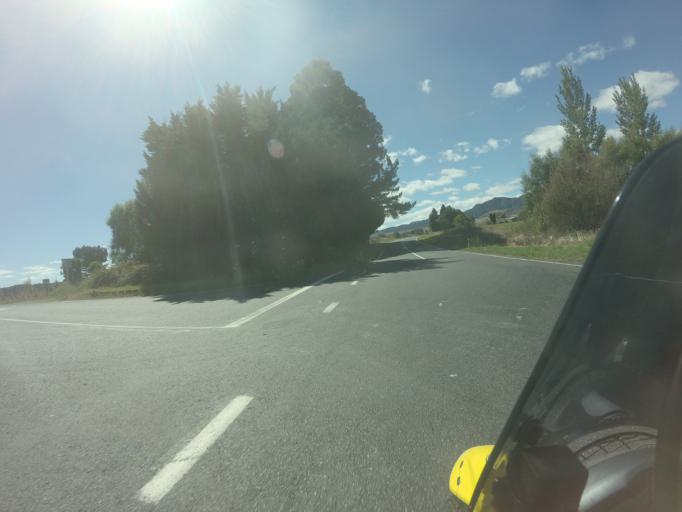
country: NZ
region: Bay of Plenty
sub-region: Whakatane District
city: Murupara
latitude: -38.3485
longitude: 176.7833
